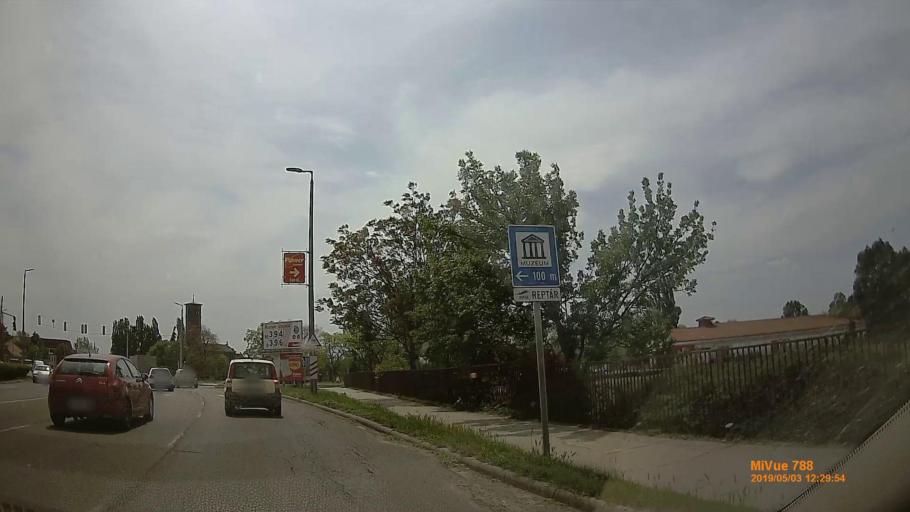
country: HU
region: Jasz-Nagykun-Szolnok
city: Szolnok
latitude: 47.1692
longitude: 20.1750
